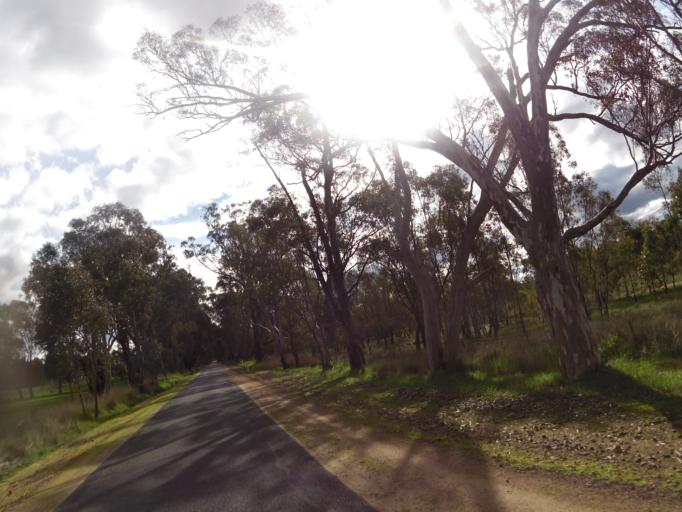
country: AU
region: Victoria
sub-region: Benalla
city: Benalla
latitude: -36.6713
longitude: 145.9332
